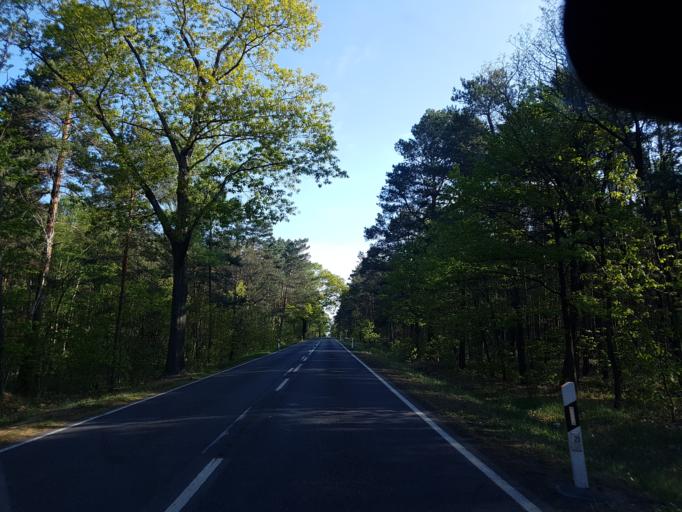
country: DE
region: Brandenburg
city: Altdobern
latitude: 51.6238
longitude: 14.0262
